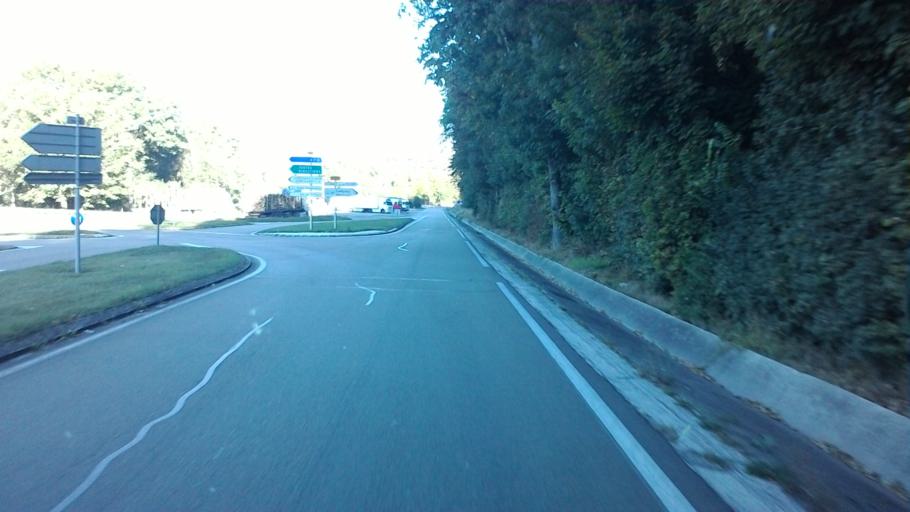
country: FR
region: Champagne-Ardenne
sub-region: Departement de la Haute-Marne
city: Chaumont
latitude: 48.1134
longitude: 5.1225
